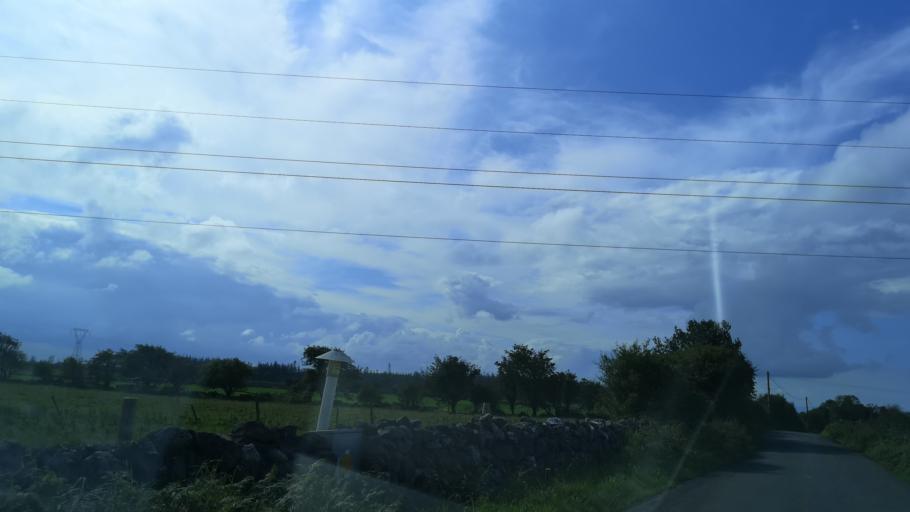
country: IE
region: Connaught
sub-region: County Galway
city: Athenry
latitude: 53.3018
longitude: -8.8160
